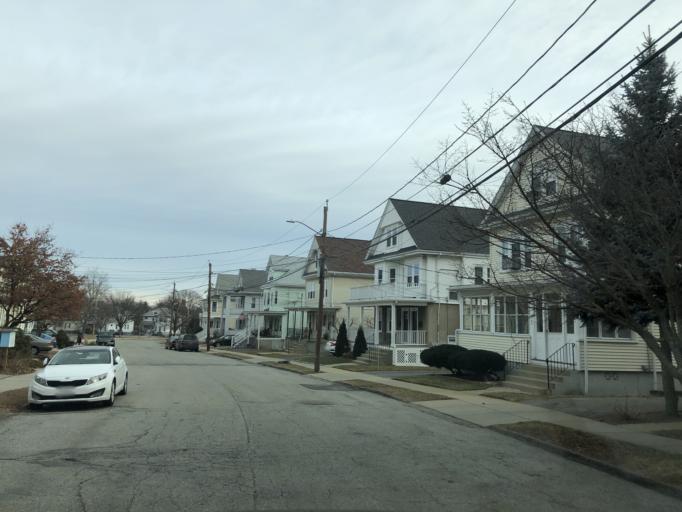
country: US
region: Massachusetts
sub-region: Middlesex County
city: Watertown
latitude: 42.3675
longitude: -71.1686
